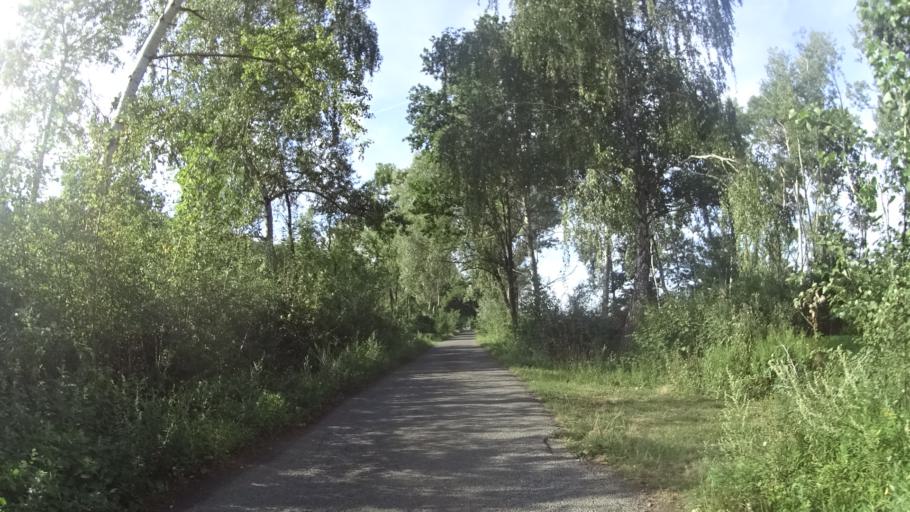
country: AT
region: Lower Austria
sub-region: Politischer Bezirk Ganserndorf
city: Drosing
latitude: 48.5812
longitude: 16.9525
